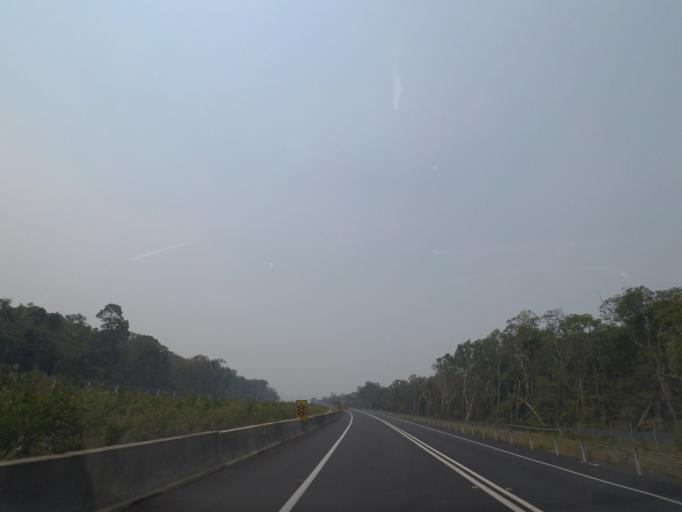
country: AU
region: New South Wales
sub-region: Ballina
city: Ballina
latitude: -28.9140
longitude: 153.4783
